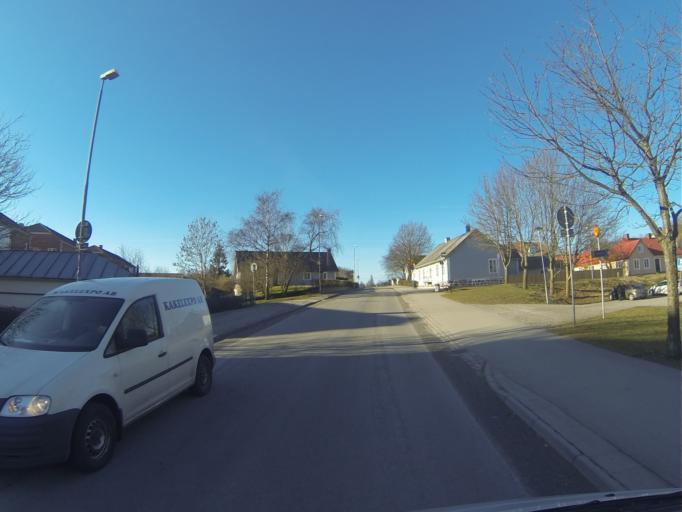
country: SE
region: Skane
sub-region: Hoors Kommun
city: Hoeoer
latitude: 55.9365
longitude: 13.5466
